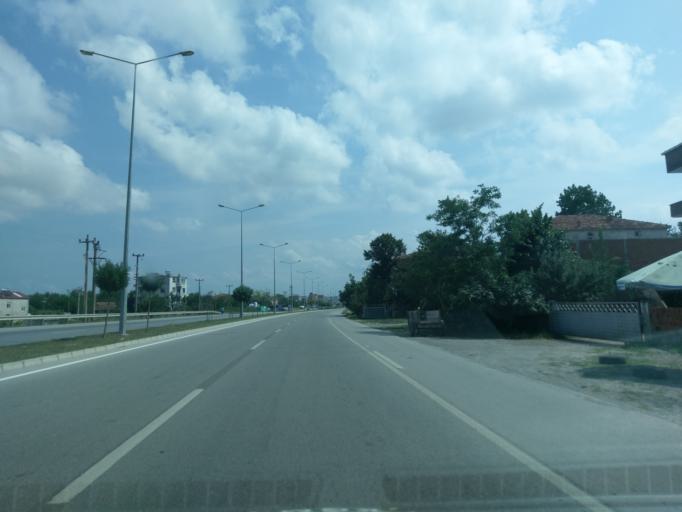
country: TR
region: Samsun
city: Bafra
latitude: 41.5720
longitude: 35.8704
